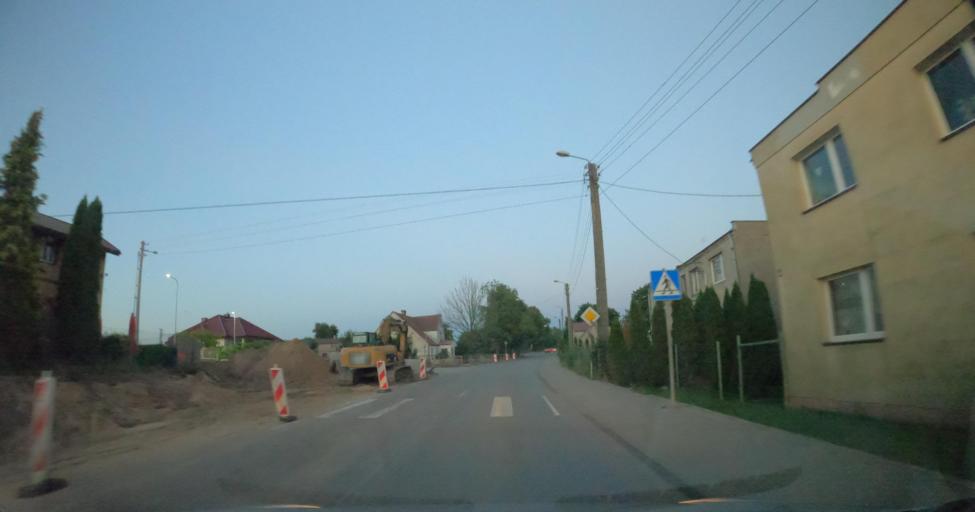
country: PL
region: Pomeranian Voivodeship
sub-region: Powiat wejherowski
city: Szemud
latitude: 54.4780
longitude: 18.2677
